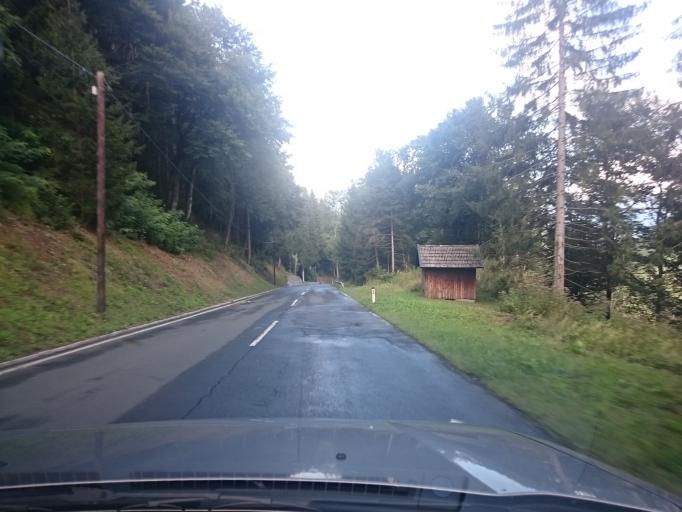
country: AT
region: Carinthia
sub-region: Politischer Bezirk Spittal an der Drau
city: Oberdrauburg
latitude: 46.6519
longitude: 12.9749
